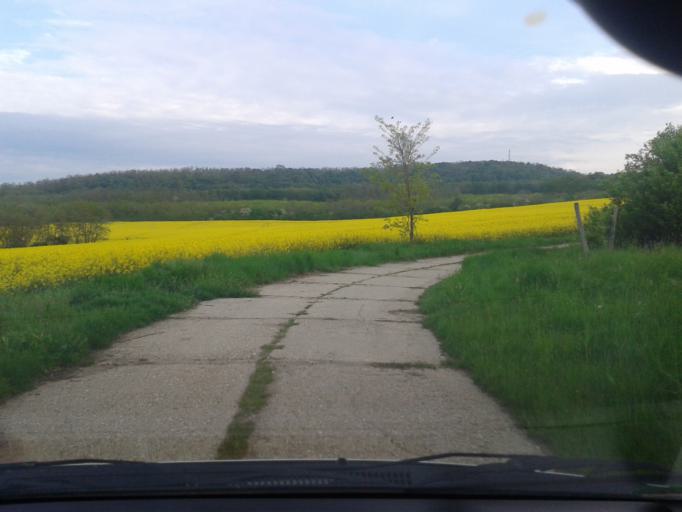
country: SK
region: Nitriansky
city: Tlmace
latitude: 48.2775
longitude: 18.5071
